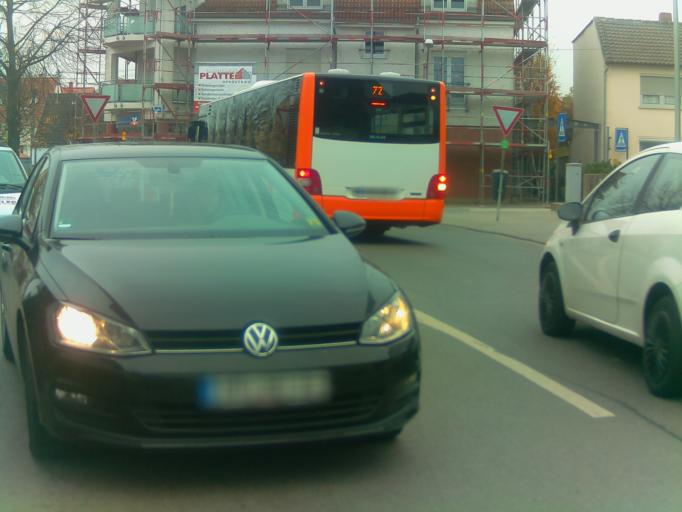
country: DE
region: Rheinland-Pfalz
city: Fussgonheim
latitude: 49.4739
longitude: 8.3288
